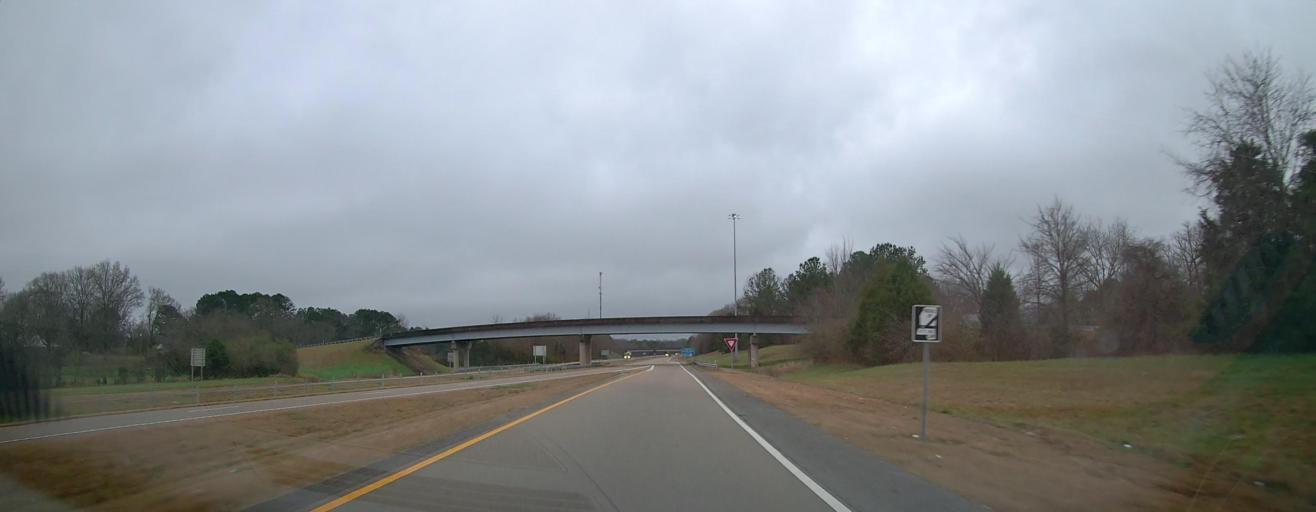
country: US
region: Mississippi
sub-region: Alcorn County
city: Corinth
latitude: 34.9290
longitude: -88.5475
